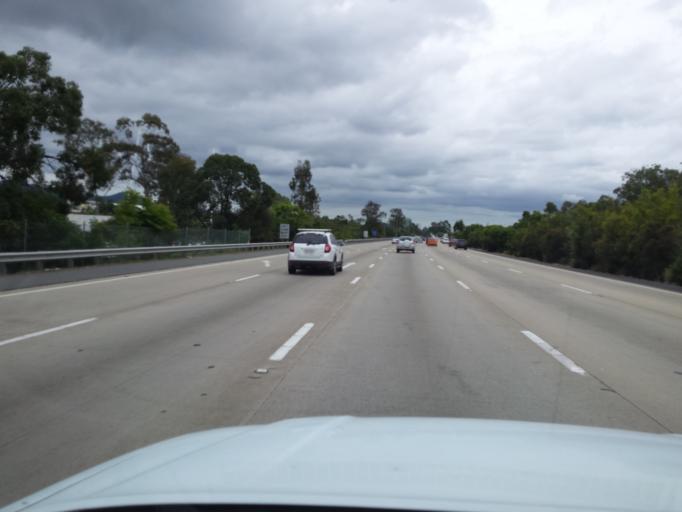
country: AU
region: Queensland
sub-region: Gold Coast
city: Upper Coomera
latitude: -27.9158
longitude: 153.3204
